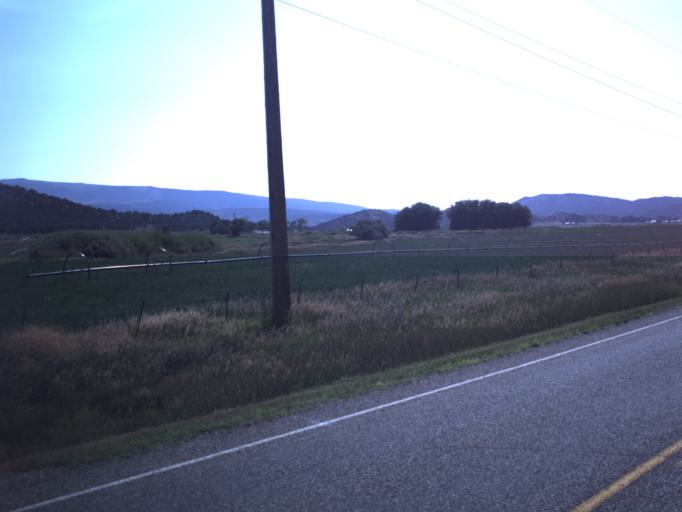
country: US
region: Utah
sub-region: Duchesne County
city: Duchesne
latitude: 40.3819
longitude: -110.7393
